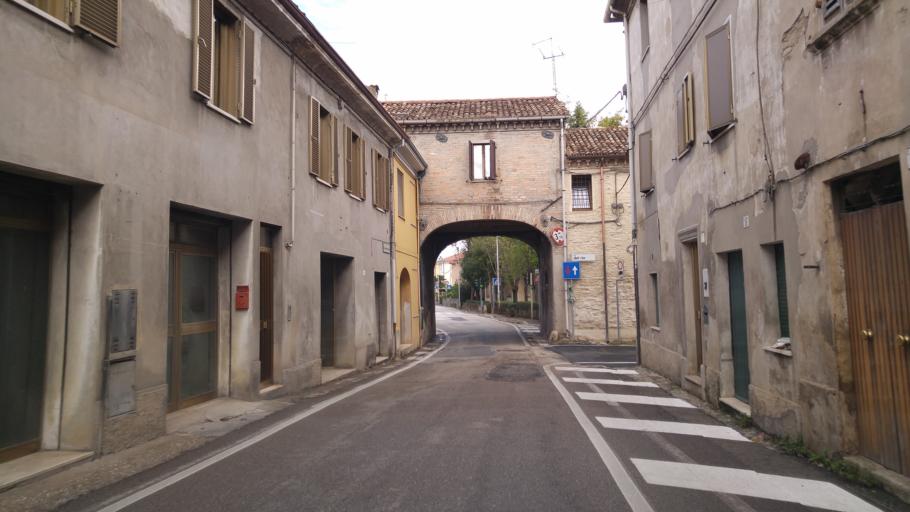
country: IT
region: The Marches
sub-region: Provincia di Pesaro e Urbino
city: Pesaro
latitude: 43.8824
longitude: 12.9012
